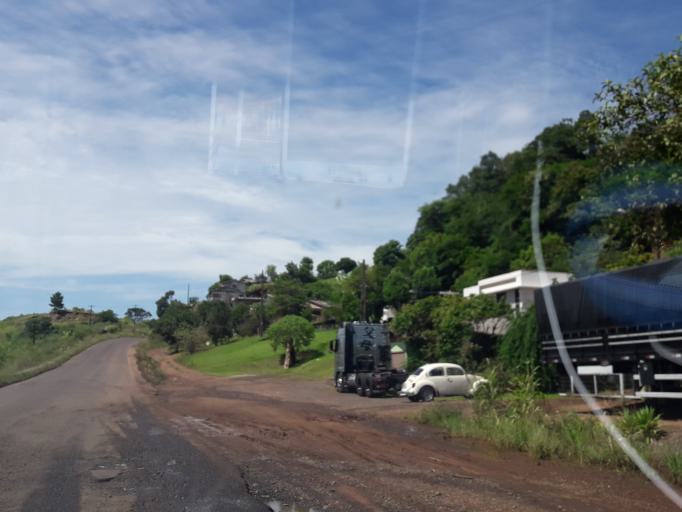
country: AR
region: Misiones
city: Bernardo de Irigoyen
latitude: -26.6068
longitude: -53.5170
